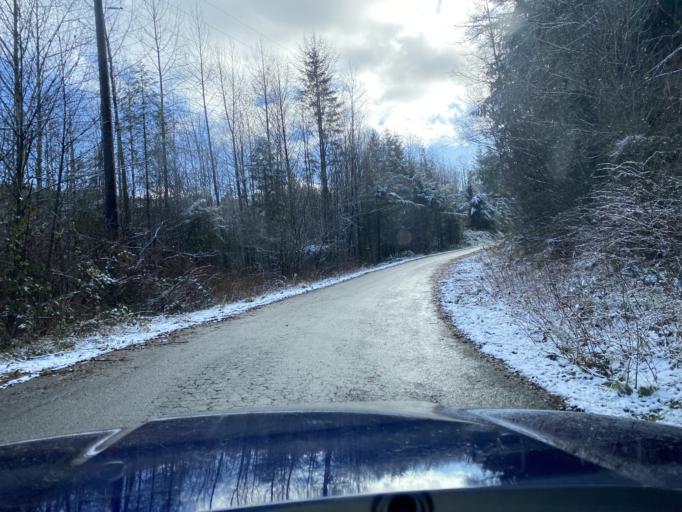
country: US
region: Washington
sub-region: King County
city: Snoqualmie
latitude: 47.5039
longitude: -121.8792
